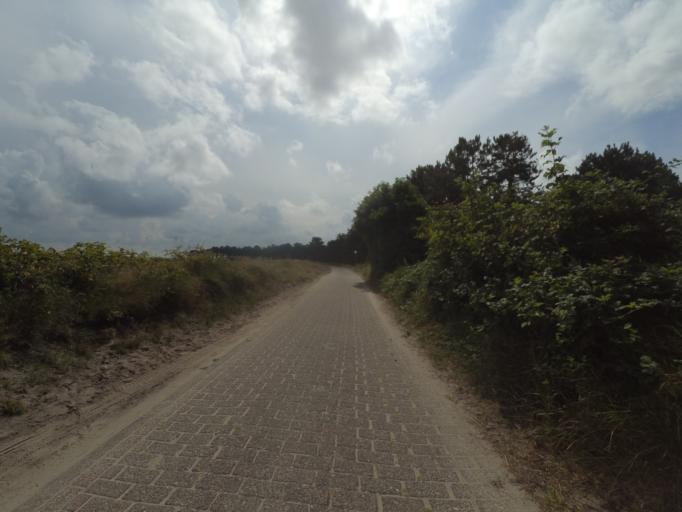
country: NL
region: North Holland
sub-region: Gemeente Texel
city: Den Burg
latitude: 53.0206
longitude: 4.7487
